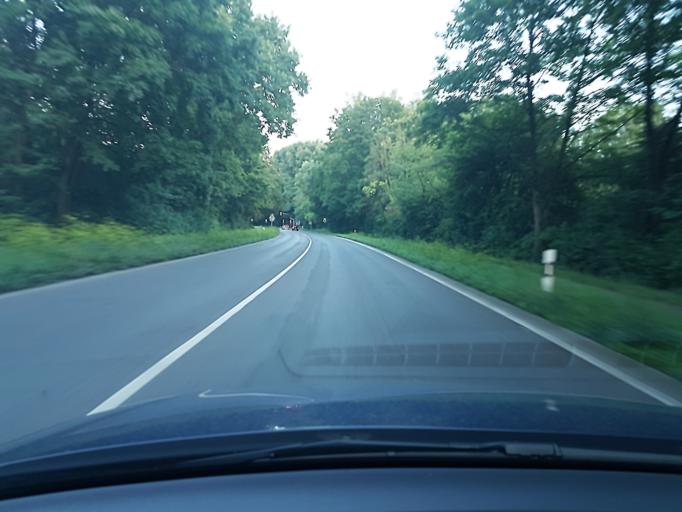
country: DE
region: North Rhine-Westphalia
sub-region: Regierungsbezirk Dusseldorf
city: Erkrath
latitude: 51.2020
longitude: 6.8847
